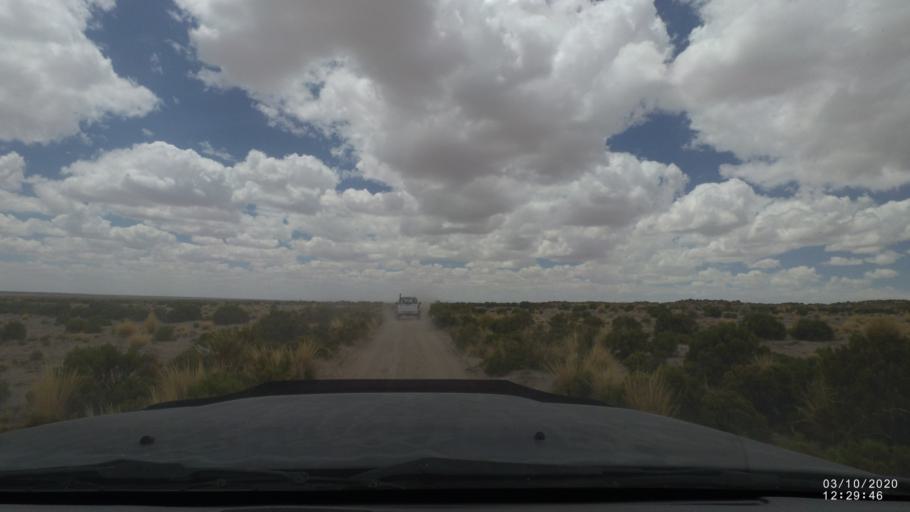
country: BO
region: Oruro
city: Poopo
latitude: -18.6884
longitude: -67.5465
